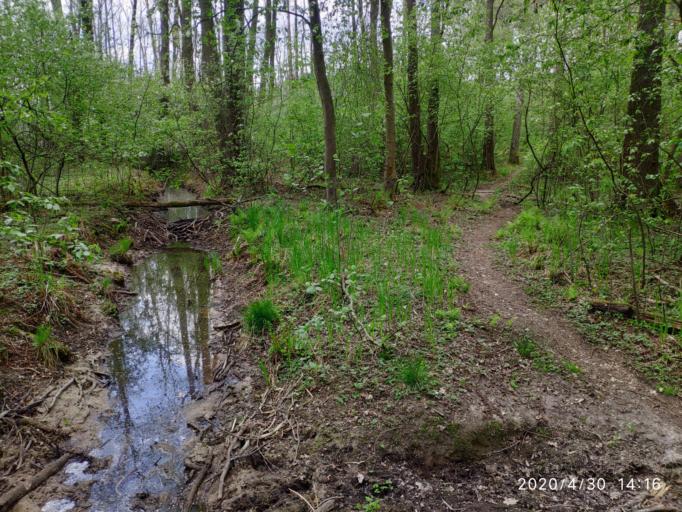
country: PL
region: Lubusz
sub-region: Powiat zielonogorski
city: Trzebiechow
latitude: 52.0695
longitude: 15.7381
